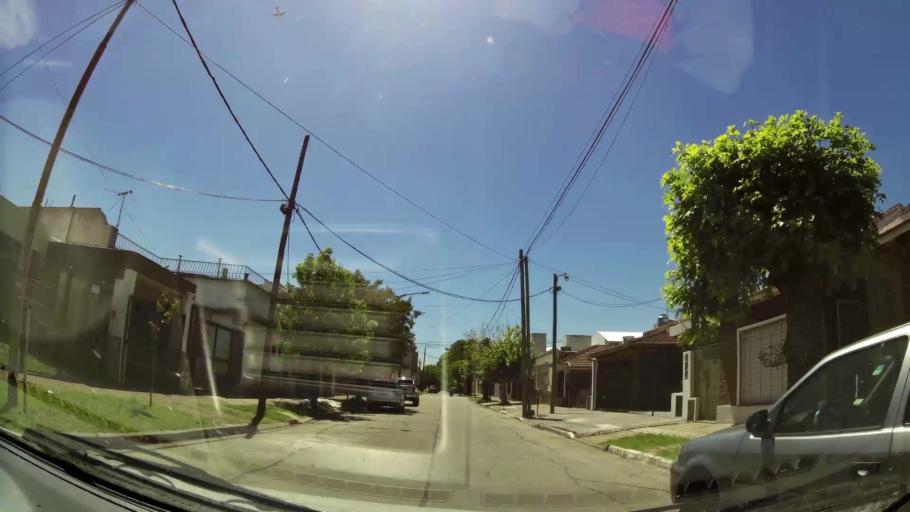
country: AR
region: Buenos Aires
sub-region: Partido de Quilmes
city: Quilmes
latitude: -34.7265
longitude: -58.2718
